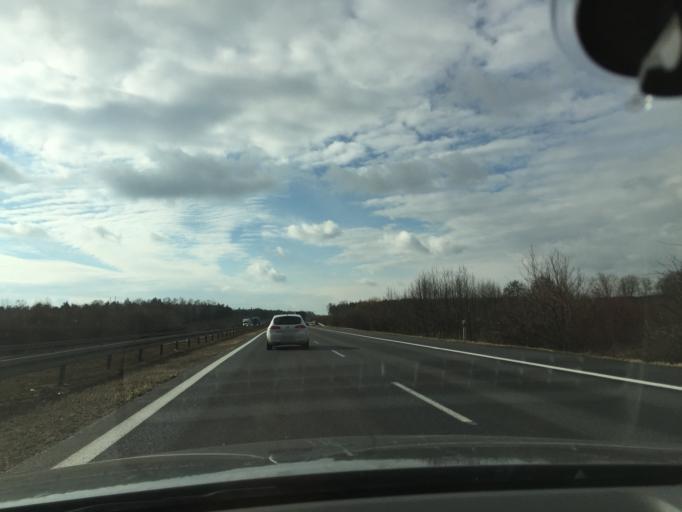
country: PL
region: Lodz Voivodeship
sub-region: Powiat radomszczanski
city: Kamiensk
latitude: 51.2530
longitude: 19.5271
